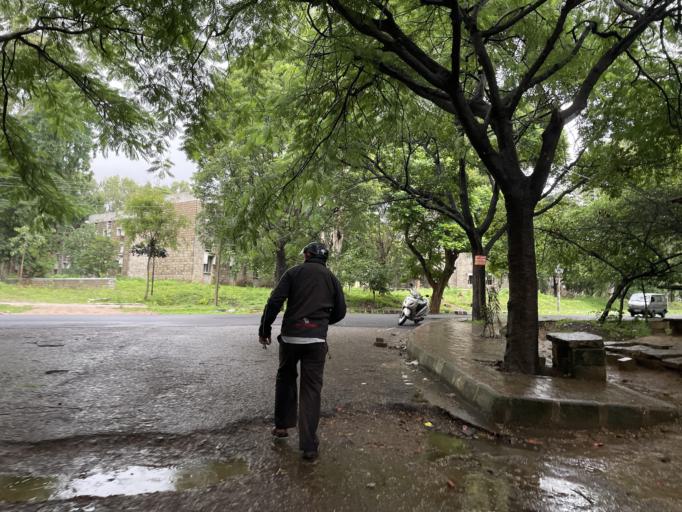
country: IN
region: Karnataka
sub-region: Bangalore Urban
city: Bangalore
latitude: 12.9437
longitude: 77.5025
